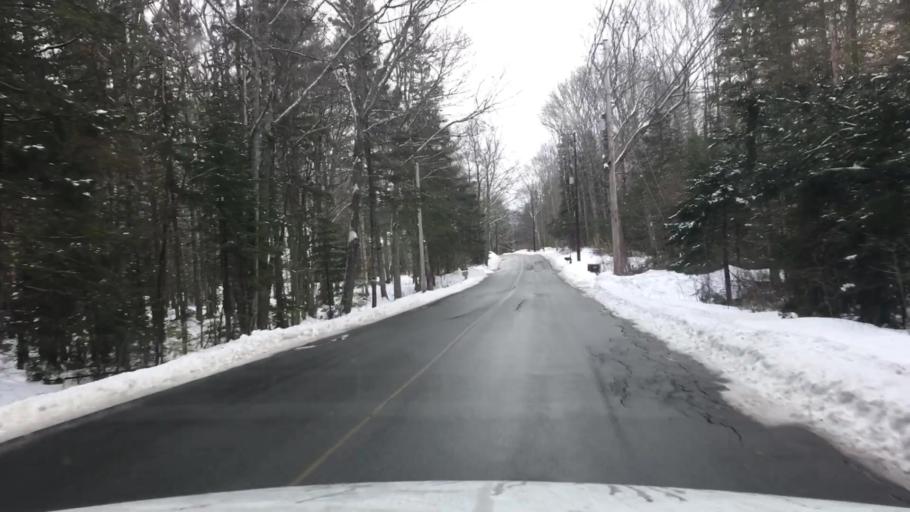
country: US
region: Maine
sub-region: Hancock County
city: Trenton
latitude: 44.4188
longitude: -68.3340
